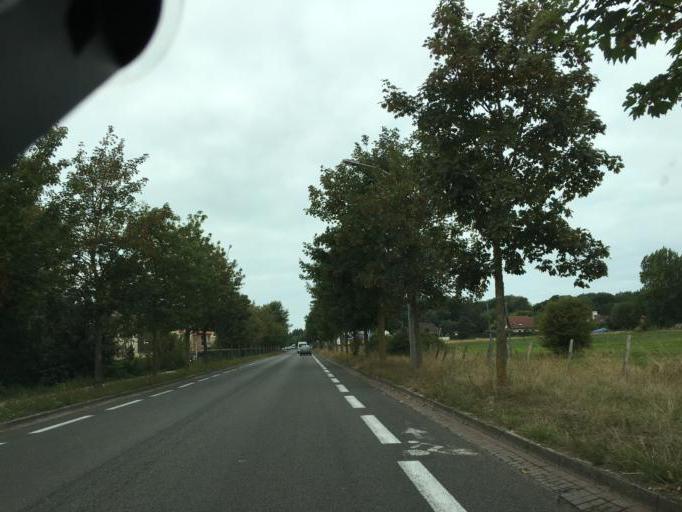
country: FR
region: Nord-Pas-de-Calais
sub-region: Departement du Pas-de-Calais
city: Berck
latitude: 50.4111
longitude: 1.5864
